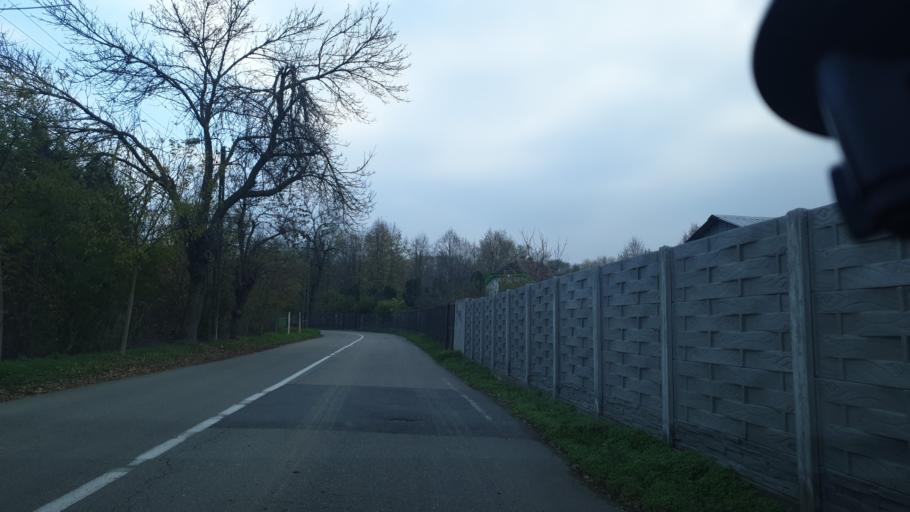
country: RO
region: Timis
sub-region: Comuna Ghiroda
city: Ghiroda
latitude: 45.7582
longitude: 21.2702
